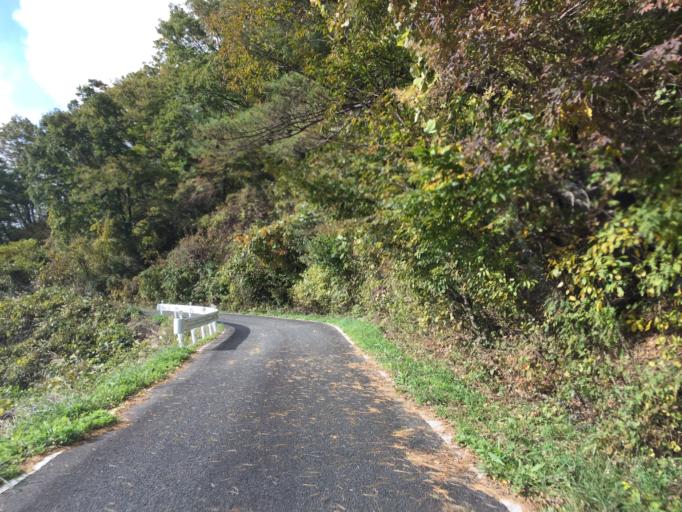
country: JP
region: Fukushima
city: Nihommatsu
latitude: 37.6784
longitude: 140.3735
